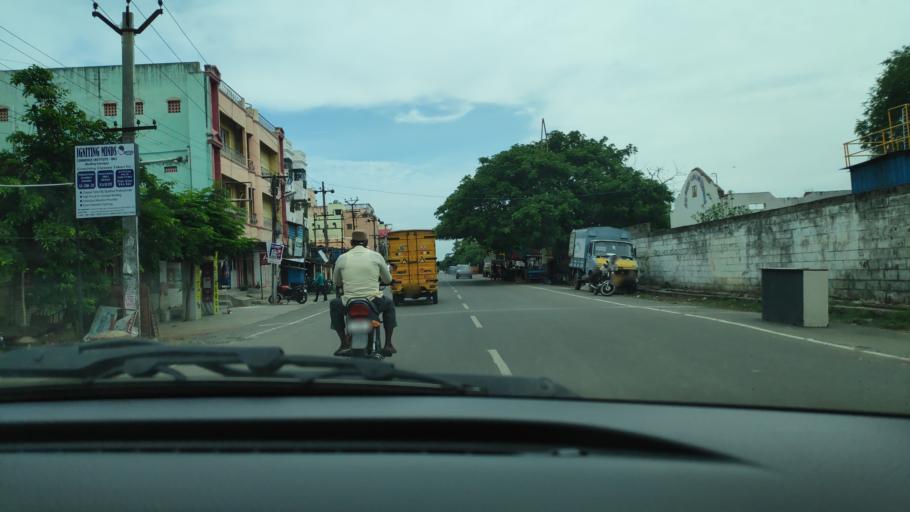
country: IN
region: Tamil Nadu
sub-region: Kancheepuram
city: Pallavaram
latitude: 12.9286
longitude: 80.1271
